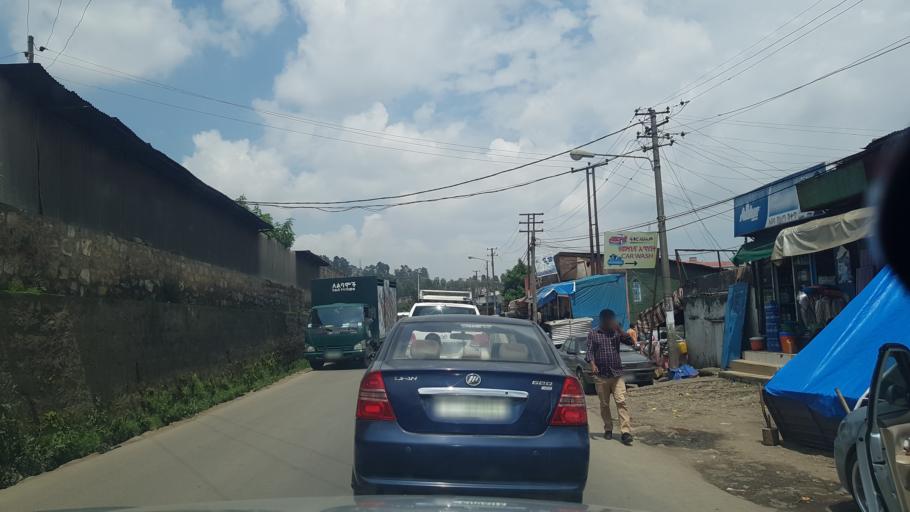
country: ET
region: Adis Abeba
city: Addis Ababa
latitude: 9.0217
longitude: 38.7547
